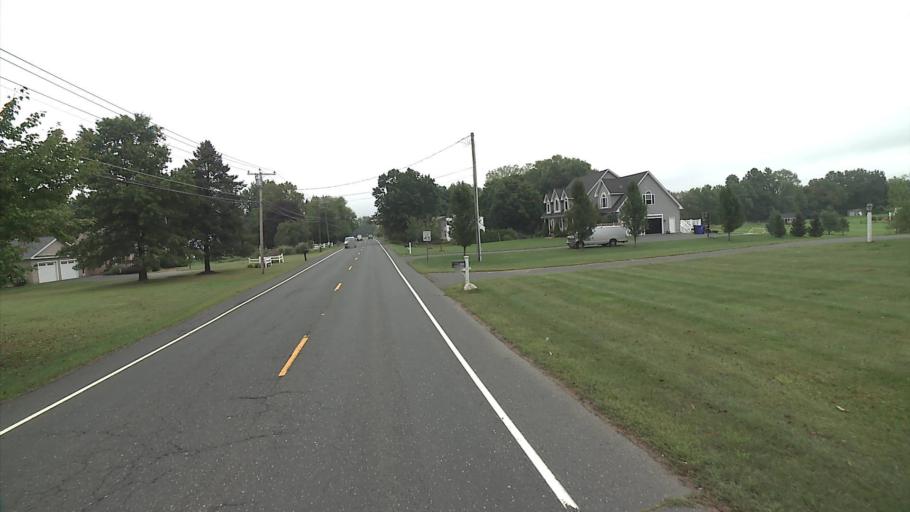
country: US
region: Connecticut
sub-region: Hartford County
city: Suffield Depot
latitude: 42.0071
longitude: -72.6438
